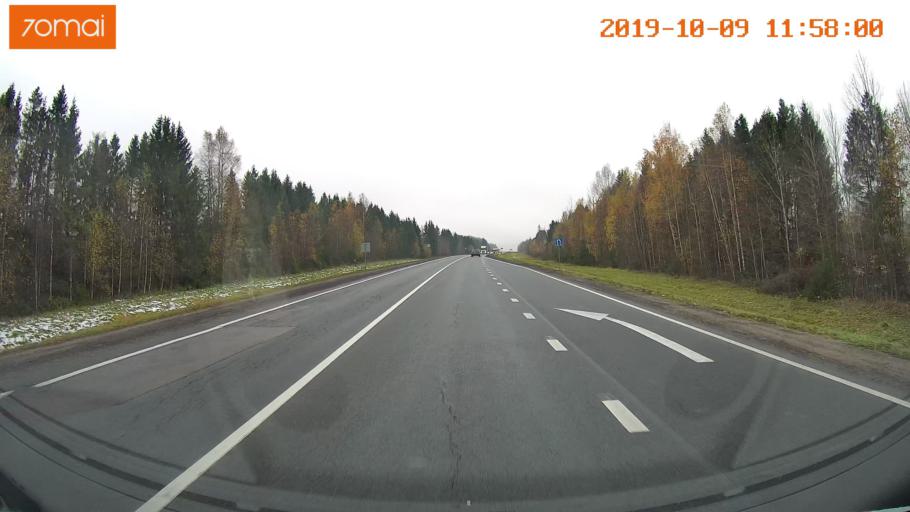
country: RU
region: Vologda
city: Gryazovets
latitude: 58.7242
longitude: 40.2957
